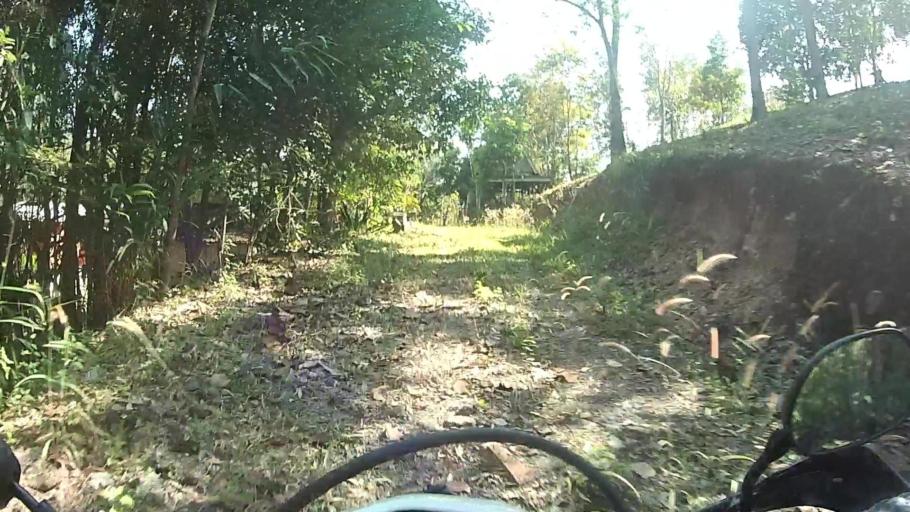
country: TH
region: Chiang Mai
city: Mae On
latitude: 18.9317
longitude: 99.2406
